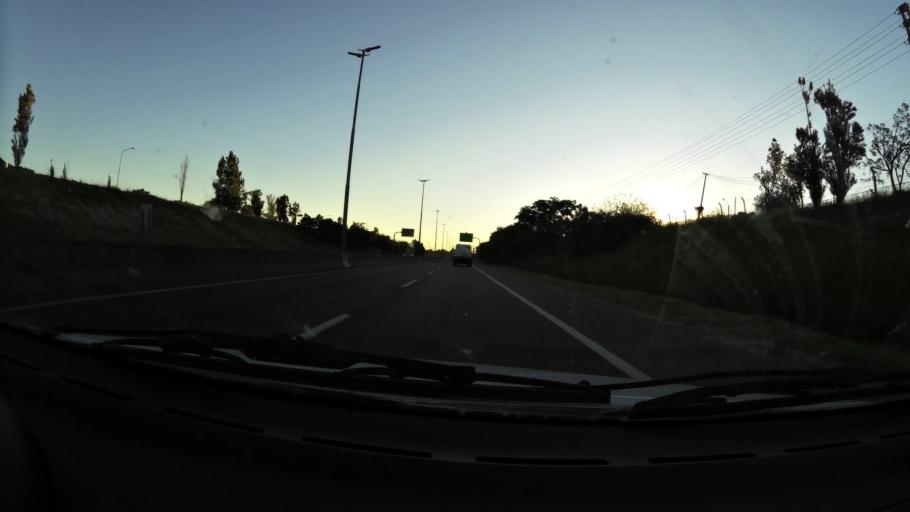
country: AR
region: Buenos Aires
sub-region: Partido de Quilmes
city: Quilmes
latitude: -34.8174
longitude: -58.1842
